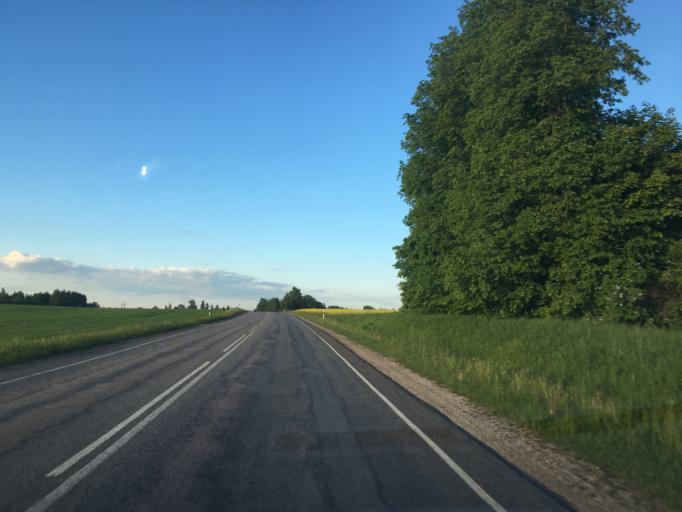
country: EE
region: Tartu
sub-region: Noo vald
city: Noo
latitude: 58.2163
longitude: 26.6150
